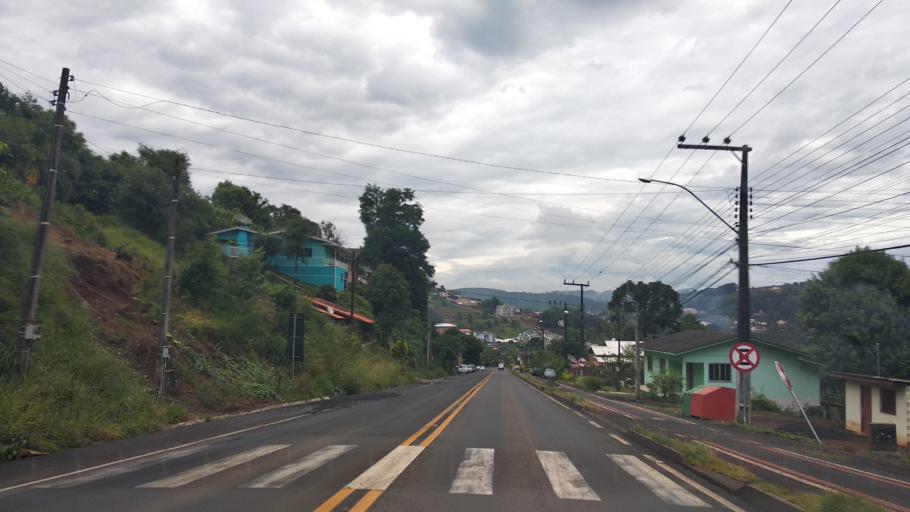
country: BR
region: Santa Catarina
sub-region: Videira
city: Videira
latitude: -27.0917
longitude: -51.2445
